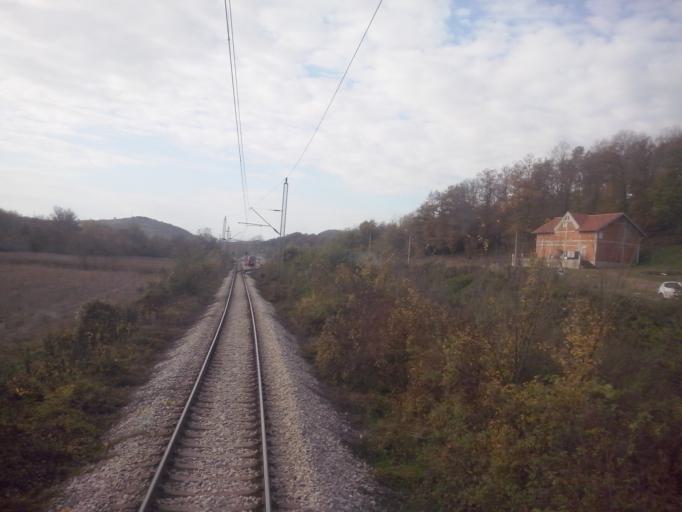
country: RS
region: Central Serbia
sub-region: Kolubarski Okrug
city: Lajkovac
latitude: 44.3513
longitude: 20.0982
